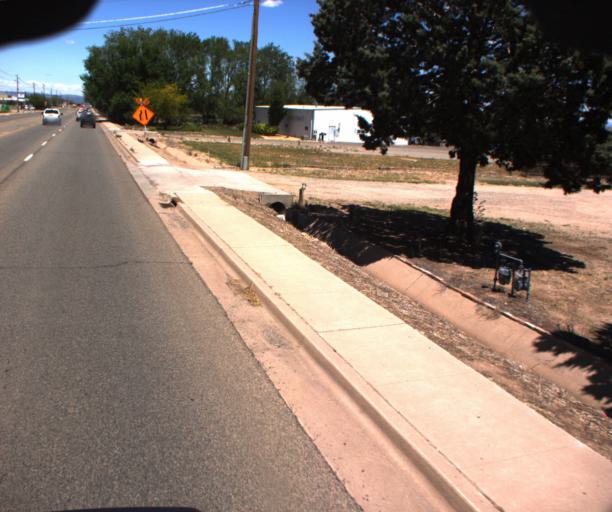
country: US
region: Arizona
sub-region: Yavapai County
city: Chino Valley
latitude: 34.7650
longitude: -112.4533
